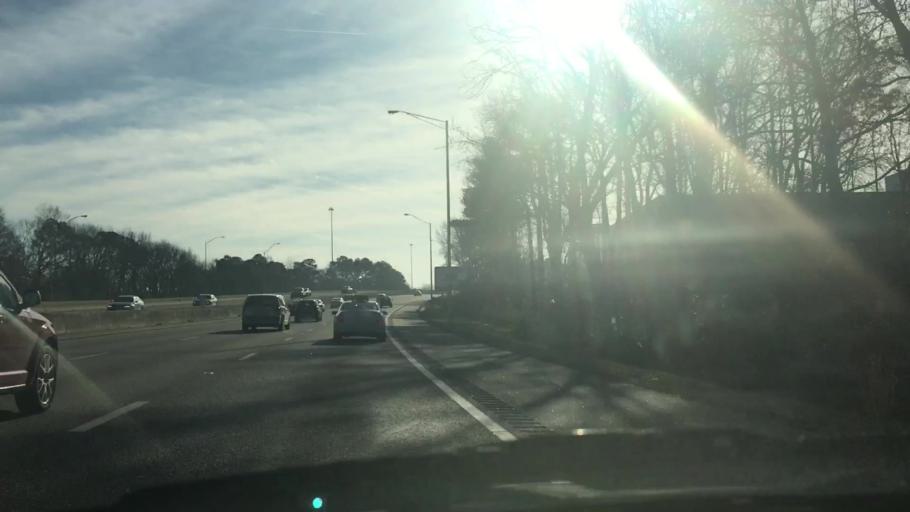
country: US
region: Virginia
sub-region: City of Norfolk
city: Norfolk
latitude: 36.8781
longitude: -76.2013
